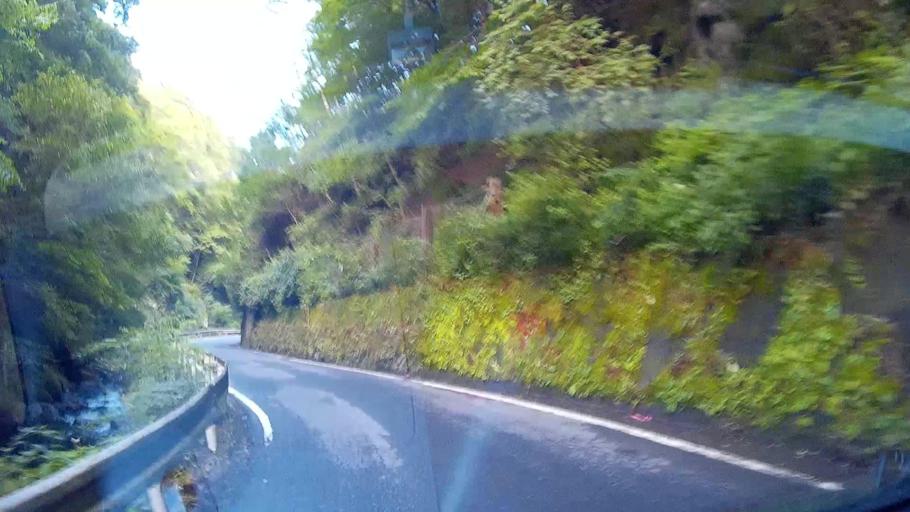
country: JP
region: Shizuoka
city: Shizuoka-shi
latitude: 35.1544
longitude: 138.2561
